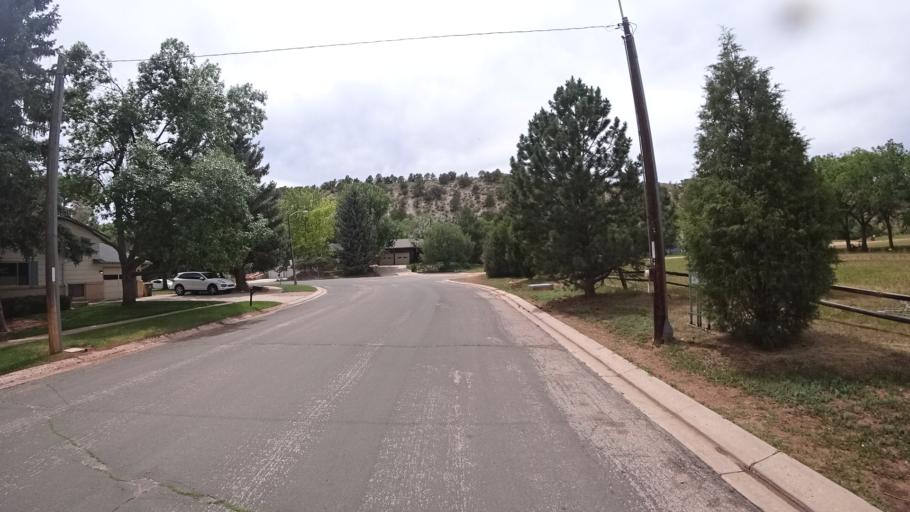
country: US
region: Colorado
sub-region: El Paso County
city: Manitou Springs
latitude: 38.8711
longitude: -104.8729
